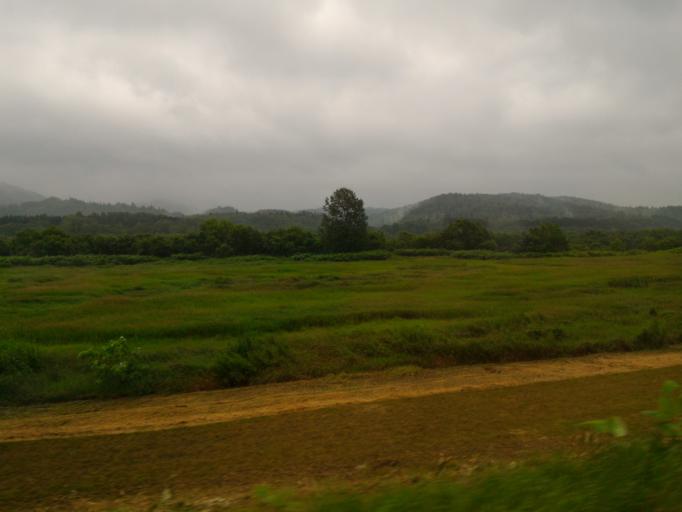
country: JP
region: Hokkaido
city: Nayoro
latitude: 44.7630
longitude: 142.0533
